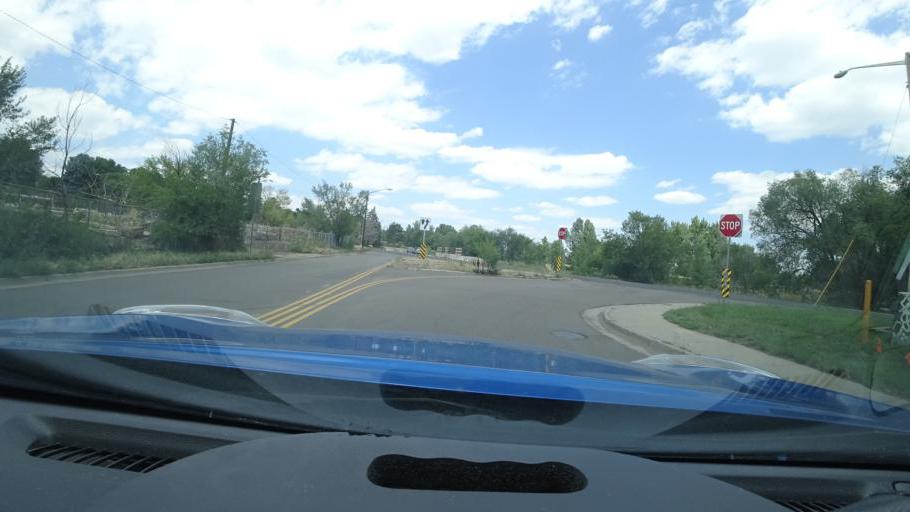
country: US
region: Colorado
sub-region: Arapahoe County
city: Englewood
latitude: 39.6815
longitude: -105.0019
